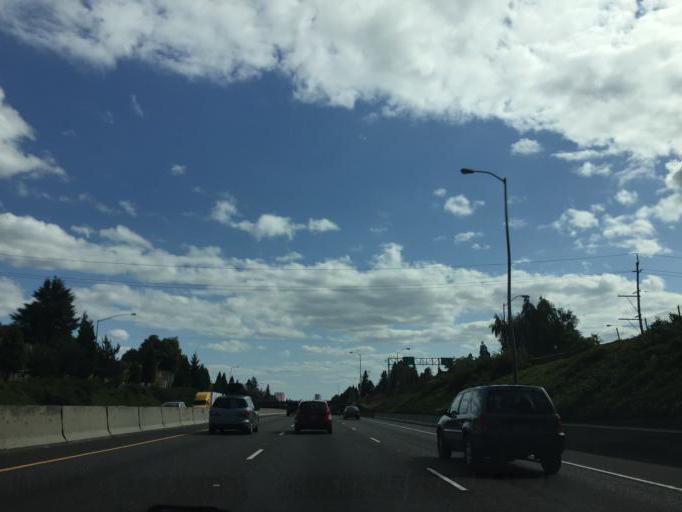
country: US
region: Oregon
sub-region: Multnomah County
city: Portland
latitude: 45.5591
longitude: -122.6787
